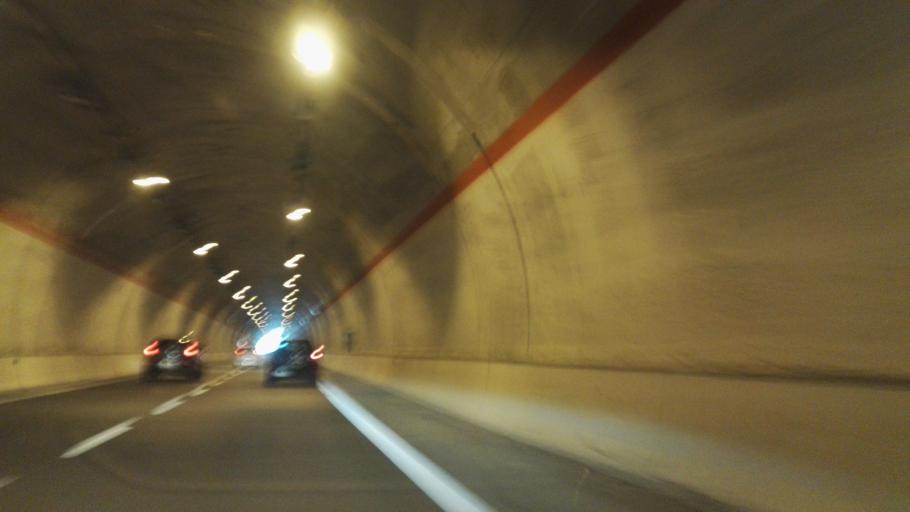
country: IT
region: Calabria
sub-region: Provincia di Catanzaro
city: Roccelletta
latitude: 38.8262
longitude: 16.5648
